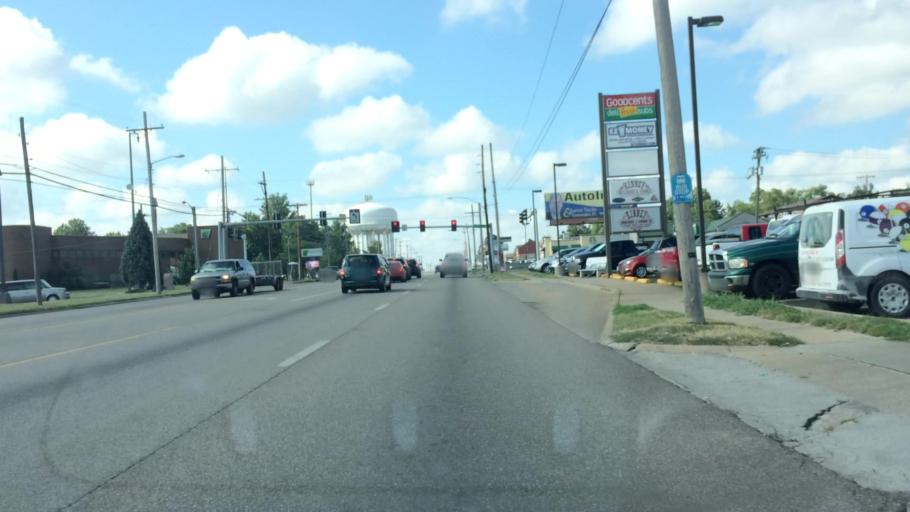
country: US
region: Missouri
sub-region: Greene County
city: Springfield
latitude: 37.2045
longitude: -93.2620
